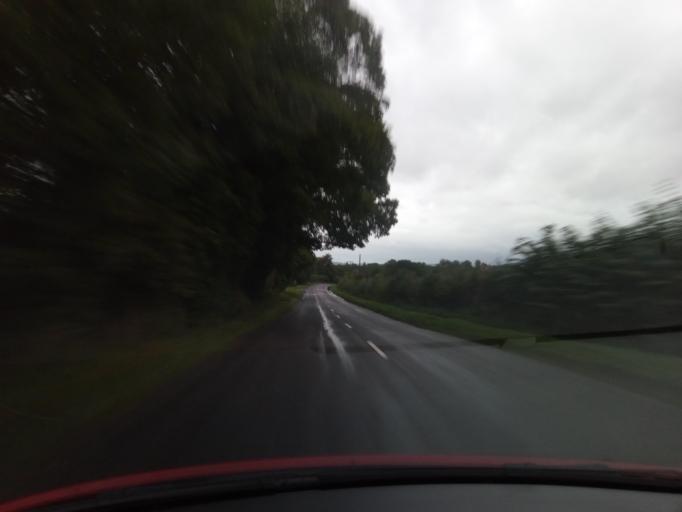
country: GB
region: England
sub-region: Darlington
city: High Coniscliffe
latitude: 54.5298
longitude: -1.6722
